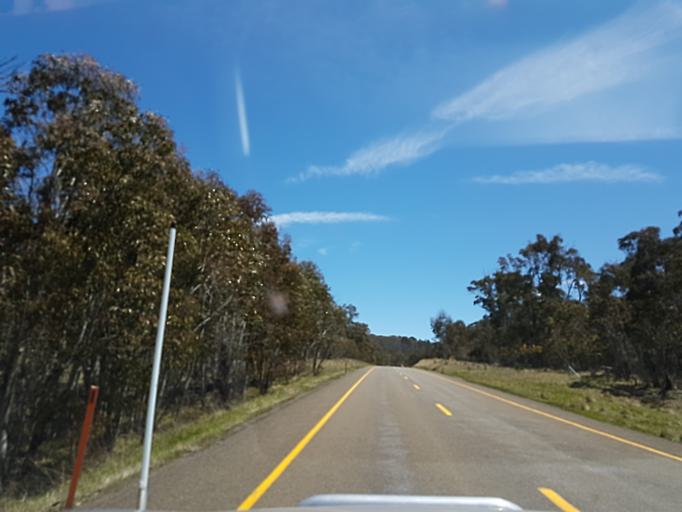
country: AU
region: Victoria
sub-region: Alpine
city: Mount Beauty
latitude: -37.0654
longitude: 147.3394
